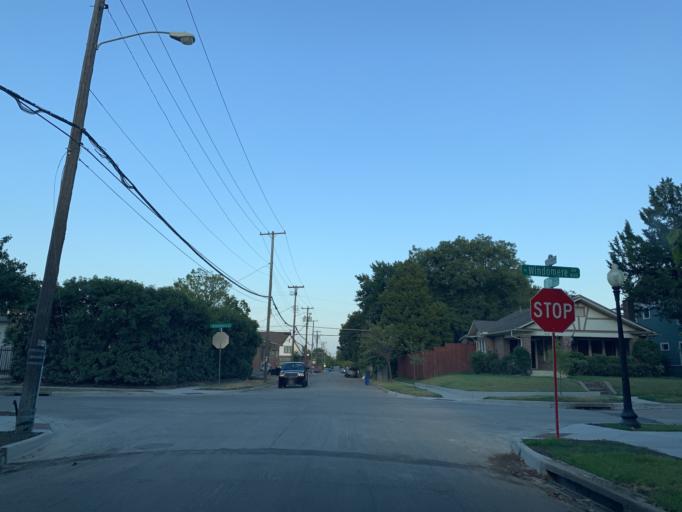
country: US
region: Texas
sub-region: Dallas County
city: Cockrell Hill
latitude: 32.7490
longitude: -96.8455
